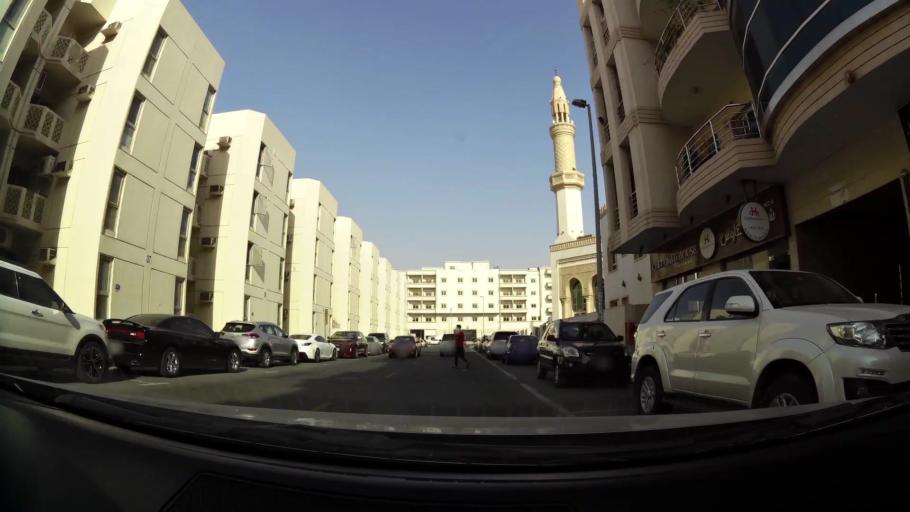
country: AE
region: Ash Shariqah
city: Sharjah
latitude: 25.2401
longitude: 55.2986
